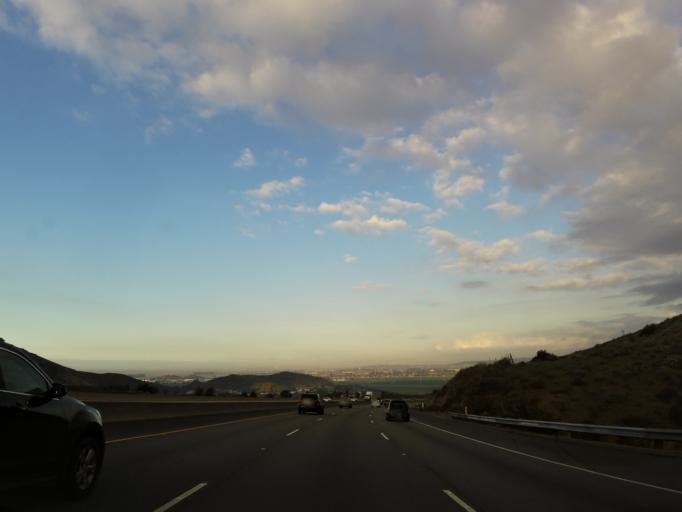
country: US
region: California
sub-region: Ventura County
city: Casa Conejo
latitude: 34.2013
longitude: -118.9762
